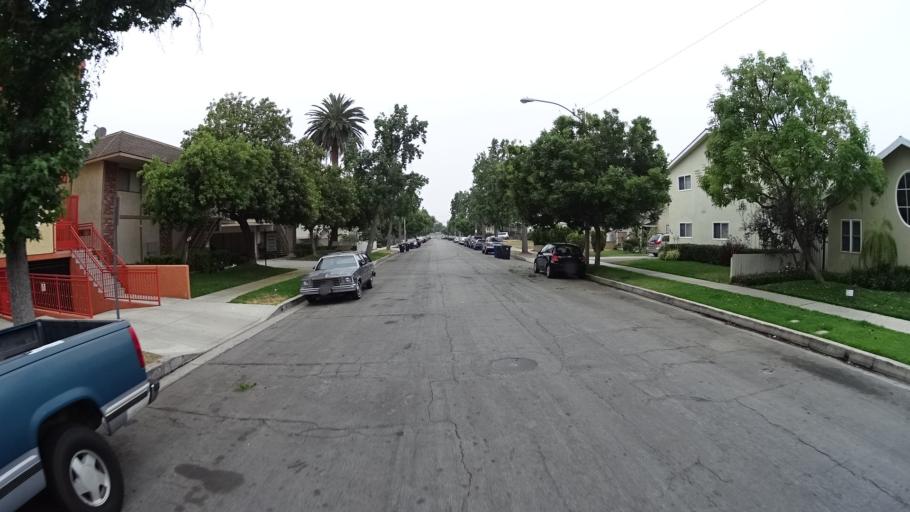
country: US
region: California
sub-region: Los Angeles County
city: Burbank
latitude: 34.1945
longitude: -118.3411
